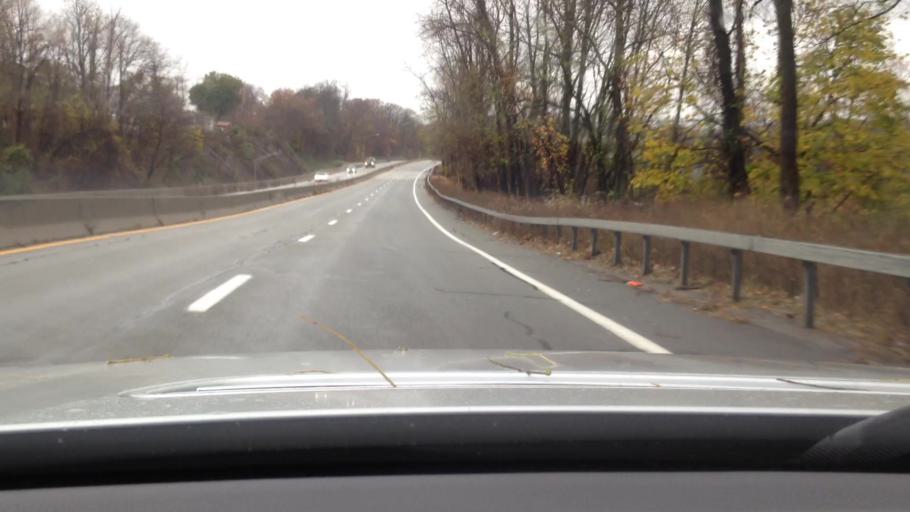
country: US
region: New York
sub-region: Westchester County
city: Peekskill
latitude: 41.2786
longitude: -73.9305
